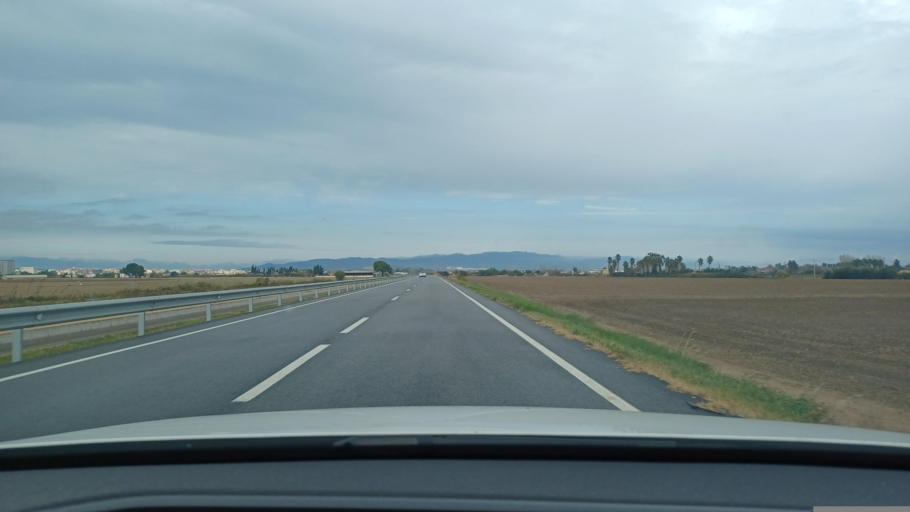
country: ES
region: Catalonia
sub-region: Provincia de Tarragona
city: Amposta
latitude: 40.6860
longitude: 0.5905
